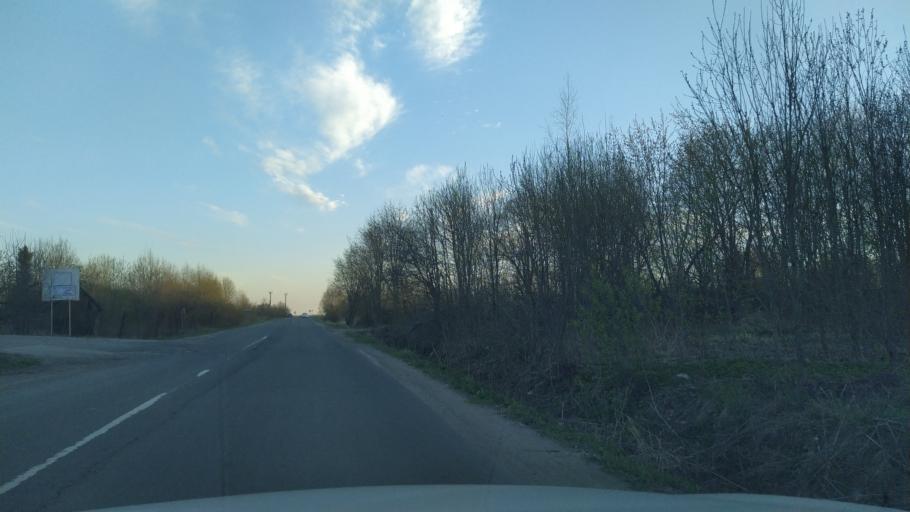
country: RU
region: St.-Petersburg
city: Pushkin
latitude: 59.6887
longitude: 30.3953
